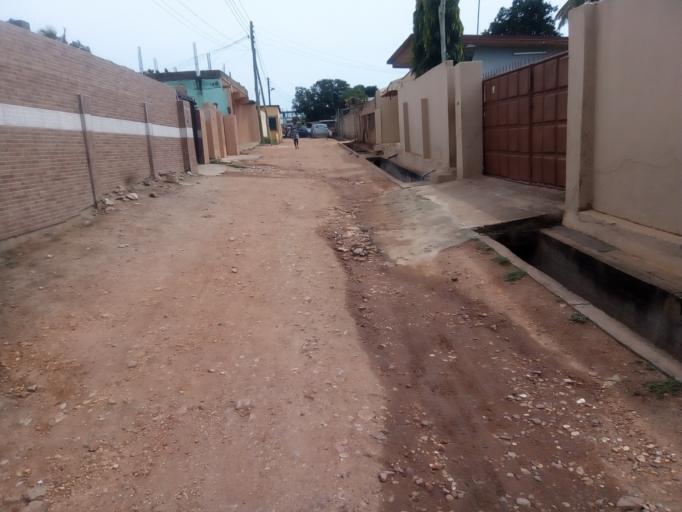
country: GH
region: Greater Accra
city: Dome
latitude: 5.6116
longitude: -0.2390
